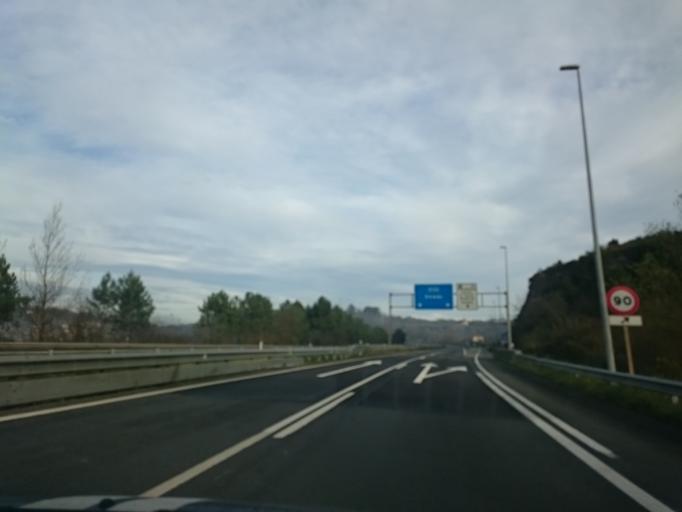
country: ES
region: Asturias
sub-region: Province of Asturias
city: Castandiello
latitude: 43.3150
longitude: -5.8677
